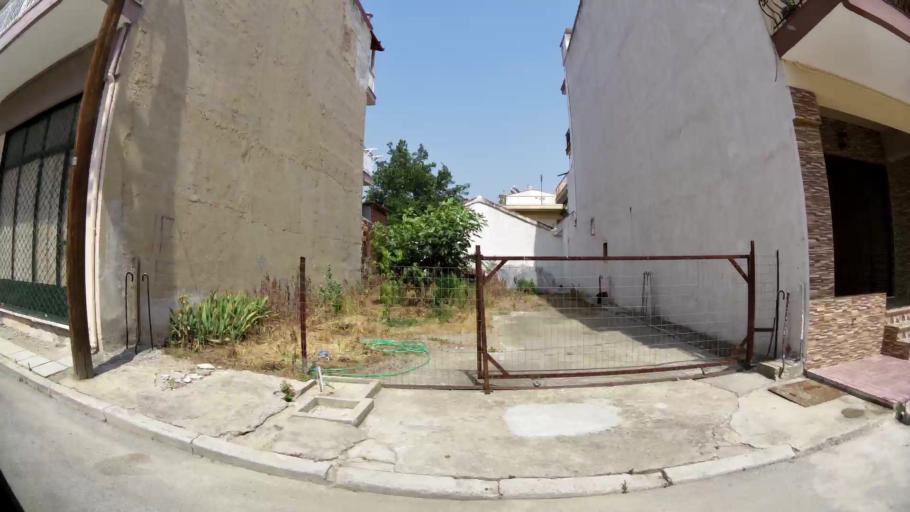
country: GR
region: Central Macedonia
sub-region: Nomos Thessalonikis
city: Nea Magnisia
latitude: 40.6877
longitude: 22.8465
